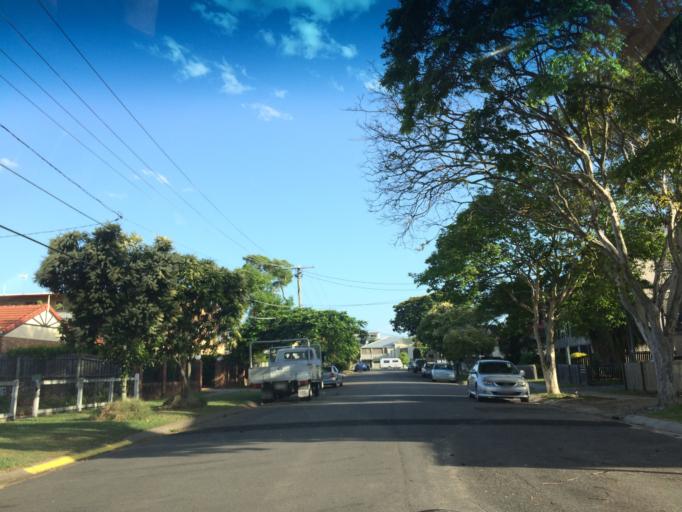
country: AU
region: Queensland
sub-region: Brisbane
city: Seven Hills
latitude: -27.4904
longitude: 153.0577
